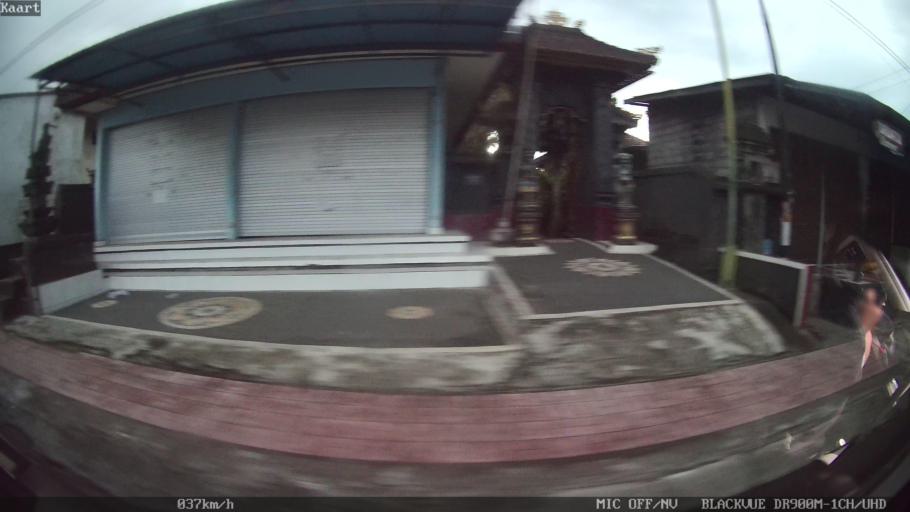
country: ID
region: Bali
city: Banjar Pasekan
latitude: -8.6174
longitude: 115.2839
